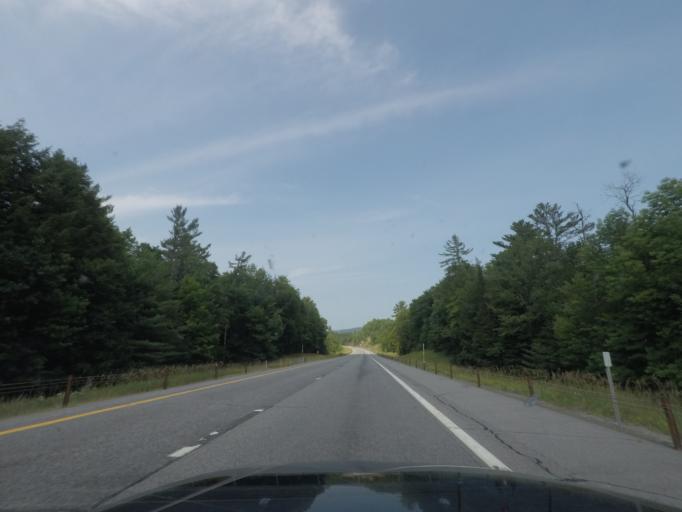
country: US
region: New York
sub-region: Essex County
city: Mineville
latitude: 44.1189
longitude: -73.5993
